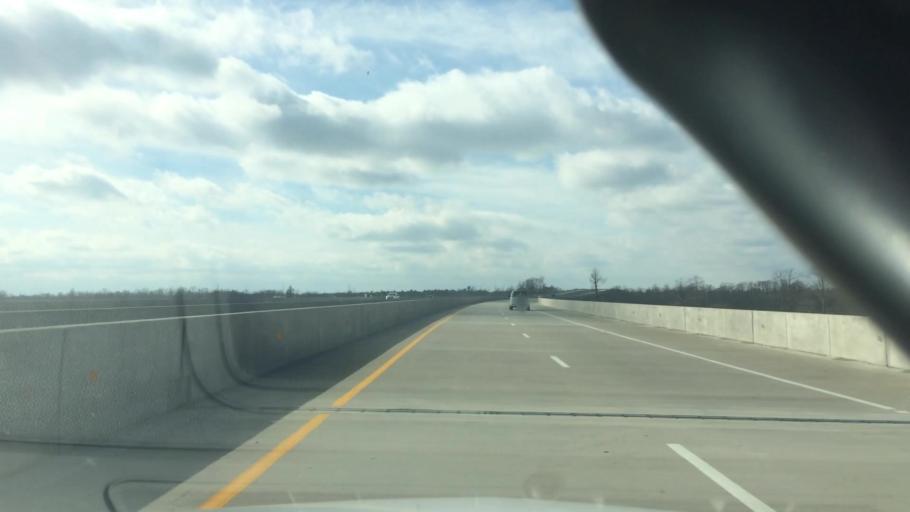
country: US
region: North Carolina
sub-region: Brunswick County
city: Navassa
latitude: 34.2741
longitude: -77.9907
